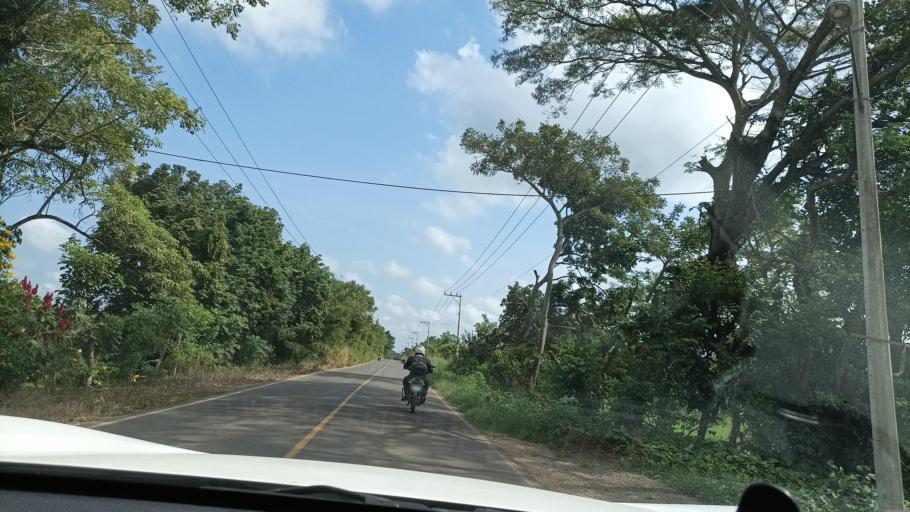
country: MX
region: Veracruz
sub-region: Chinameca
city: Chacalapa
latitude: 18.0724
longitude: -94.6909
